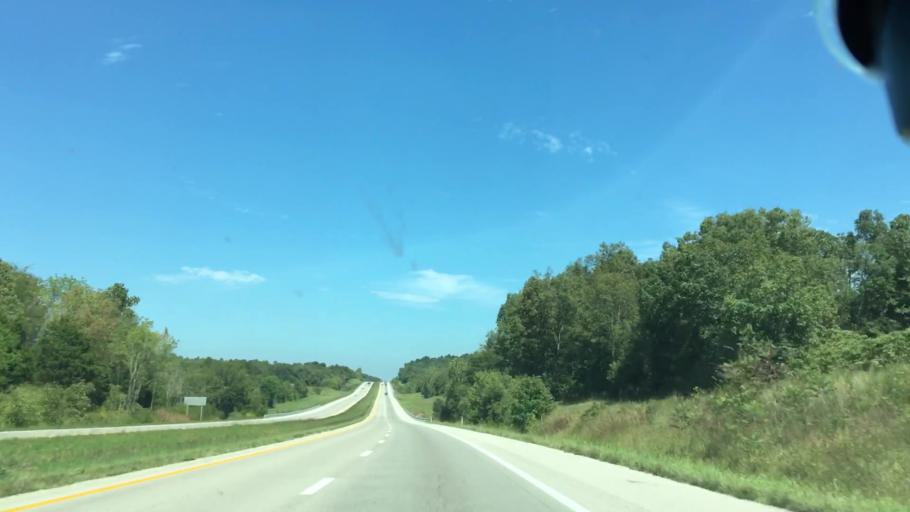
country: US
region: Kentucky
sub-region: Christian County
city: Hopkinsville
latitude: 36.9311
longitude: -87.4701
